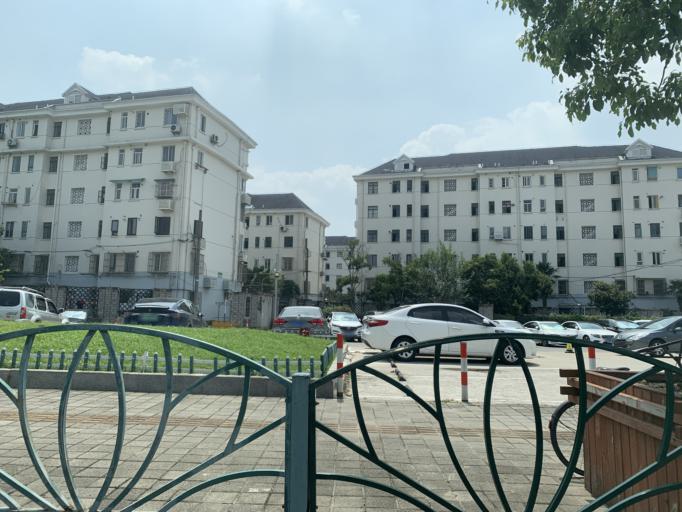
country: CN
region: Shanghai Shi
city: Luwan
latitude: 31.1845
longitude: 121.4921
